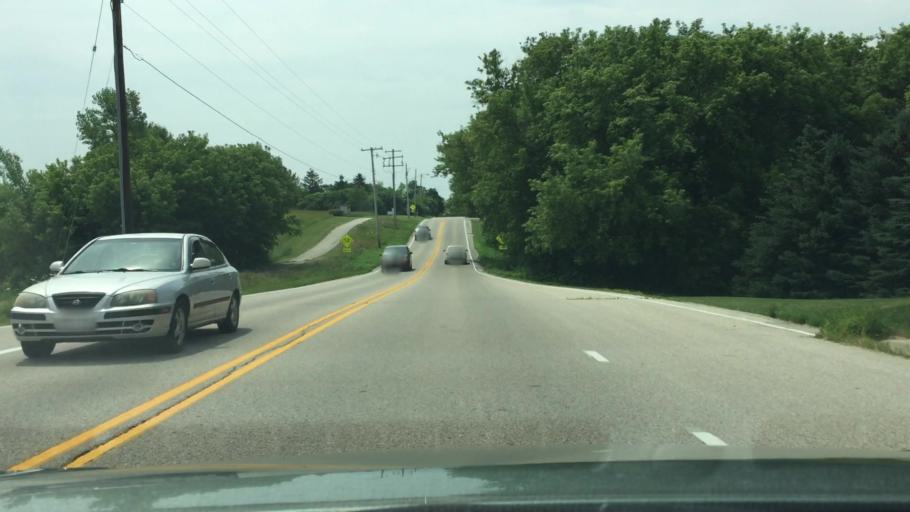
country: US
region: Wisconsin
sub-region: Waukesha County
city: Merton
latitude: 43.1362
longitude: -88.3075
